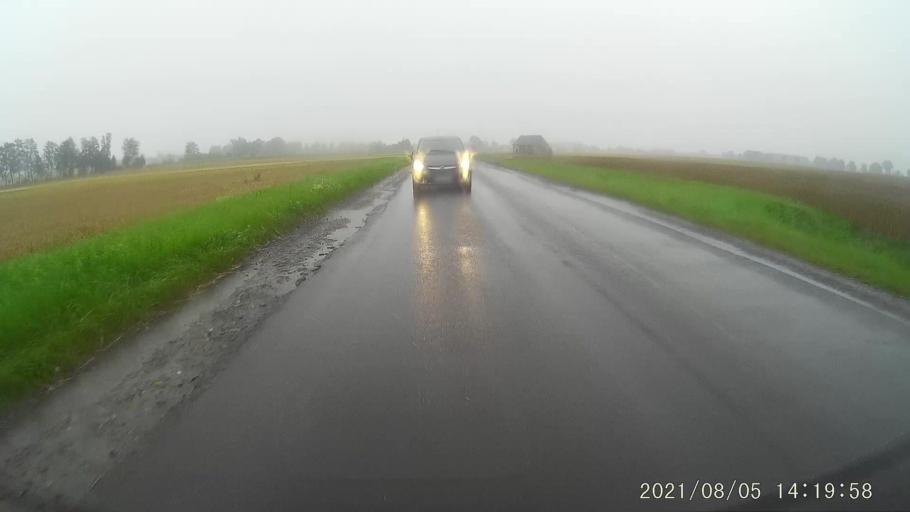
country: PL
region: Opole Voivodeship
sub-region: Powiat prudnicki
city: Biala
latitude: 50.4682
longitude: 17.6836
